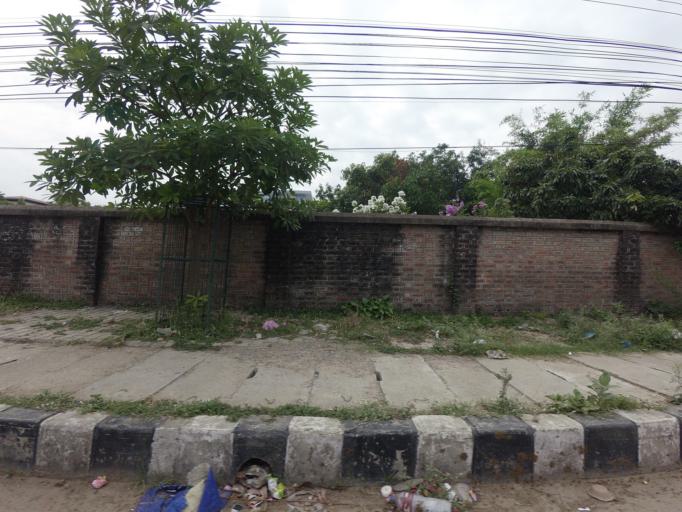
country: NP
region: Western Region
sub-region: Lumbini Zone
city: Bhairahawa
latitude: 27.4955
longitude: 83.4467
